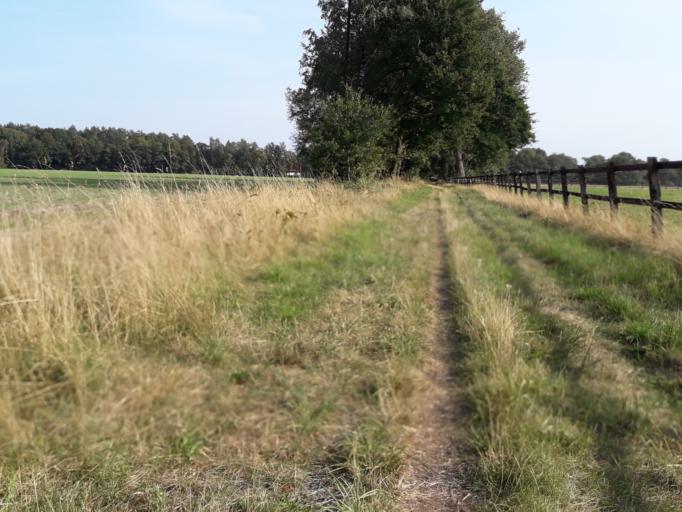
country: DE
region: North Rhine-Westphalia
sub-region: Regierungsbezirk Detmold
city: Hovelhof
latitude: 51.7885
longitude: 8.6763
